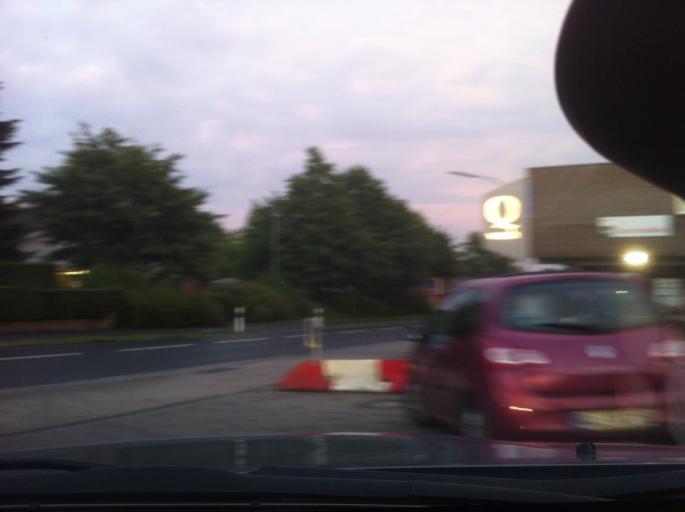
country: DE
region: North Rhine-Westphalia
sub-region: Regierungsbezirk Dusseldorf
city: Kleve
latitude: 51.7709
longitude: 6.1167
